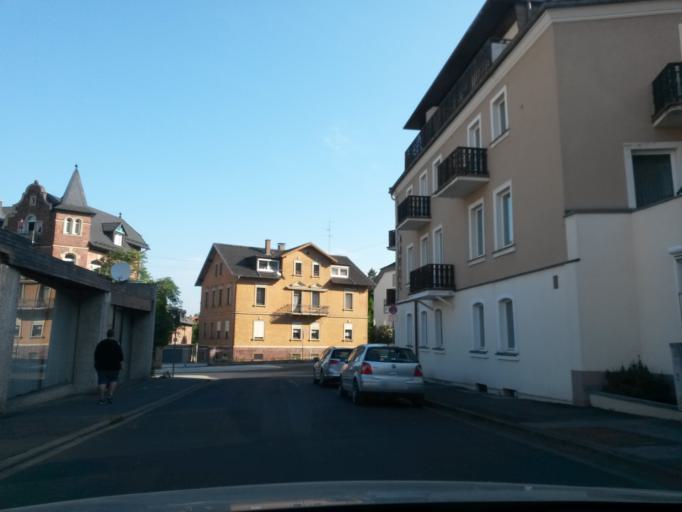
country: DE
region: Bavaria
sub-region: Regierungsbezirk Unterfranken
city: Bad Kissingen
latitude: 50.1988
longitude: 10.0823
